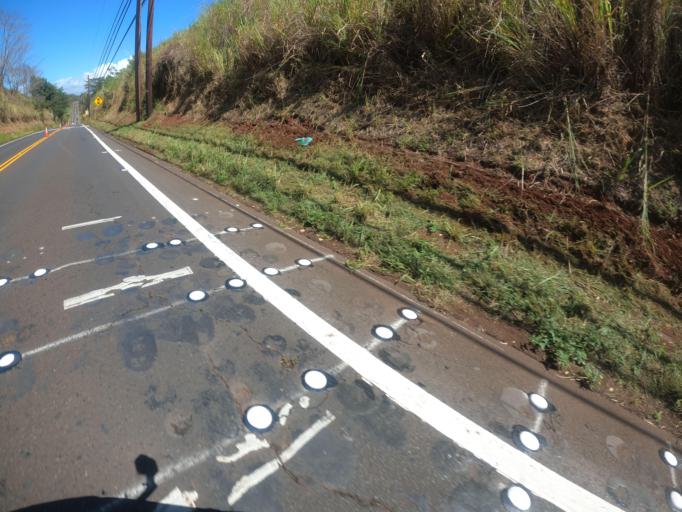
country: US
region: Hawaii
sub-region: Honolulu County
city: Schofield Barracks
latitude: 21.4736
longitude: -158.0518
